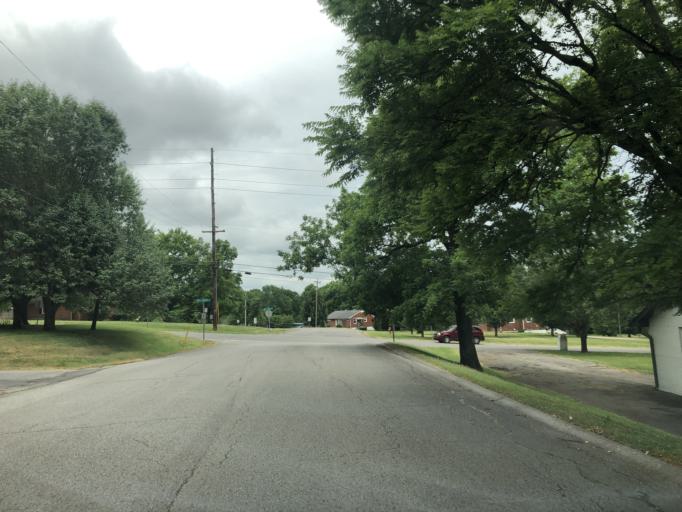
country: US
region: Tennessee
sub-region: Davidson County
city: Goodlettsville
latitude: 36.2697
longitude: -86.7633
